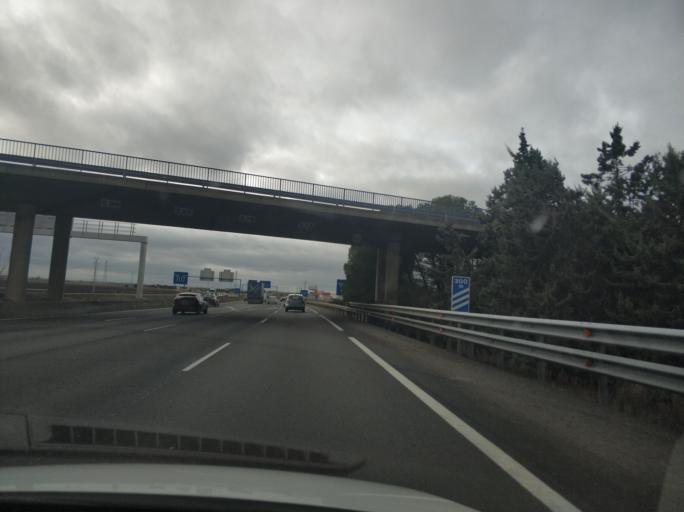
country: ES
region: Castille and Leon
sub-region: Provincia de Valladolid
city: Tordesillas
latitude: 41.5134
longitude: -5.0012
